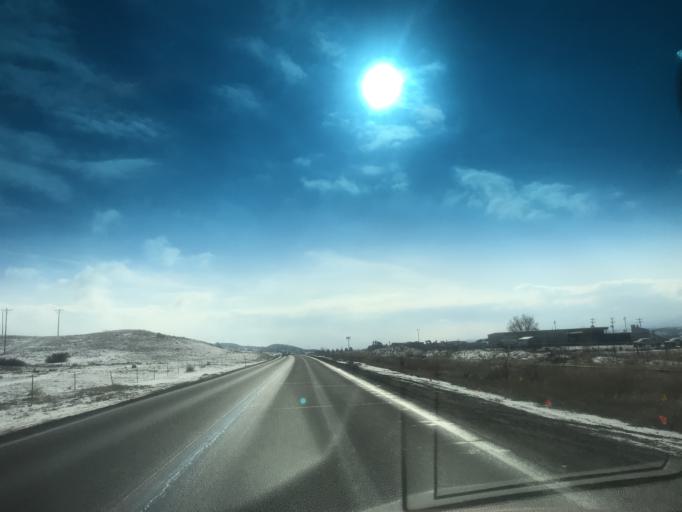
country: US
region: Colorado
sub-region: Douglas County
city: Highlands Ranch
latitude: 39.4771
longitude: -104.9919
